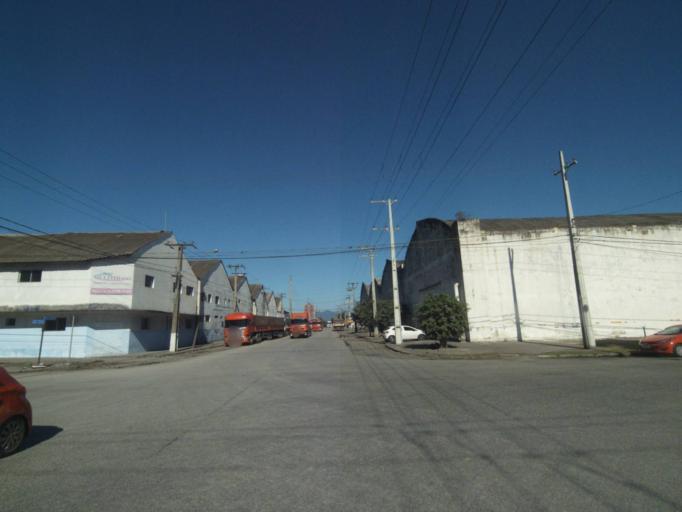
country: BR
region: Parana
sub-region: Paranagua
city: Paranagua
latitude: -25.5102
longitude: -48.5104
